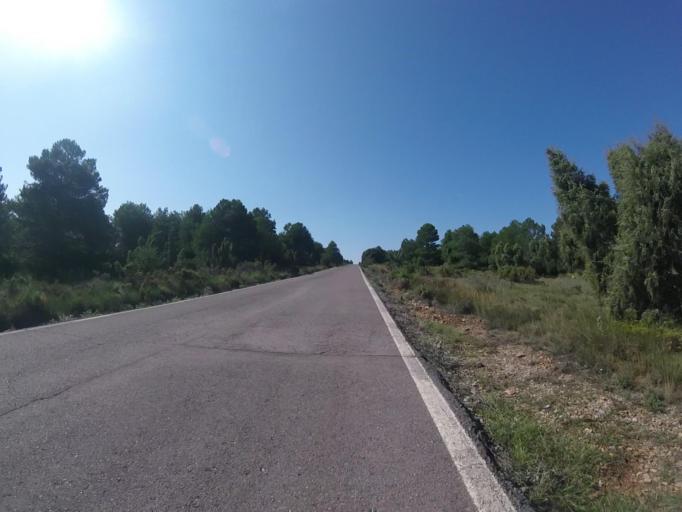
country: ES
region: Valencia
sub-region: Provincia de Castello
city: Benafigos
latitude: 40.2839
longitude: -0.2386
